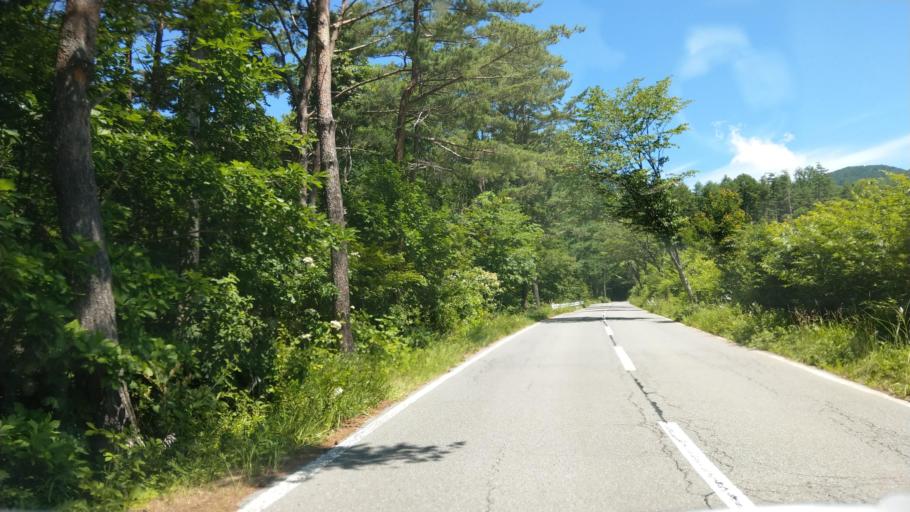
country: JP
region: Nagano
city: Komoro
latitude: 36.3818
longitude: 138.4619
